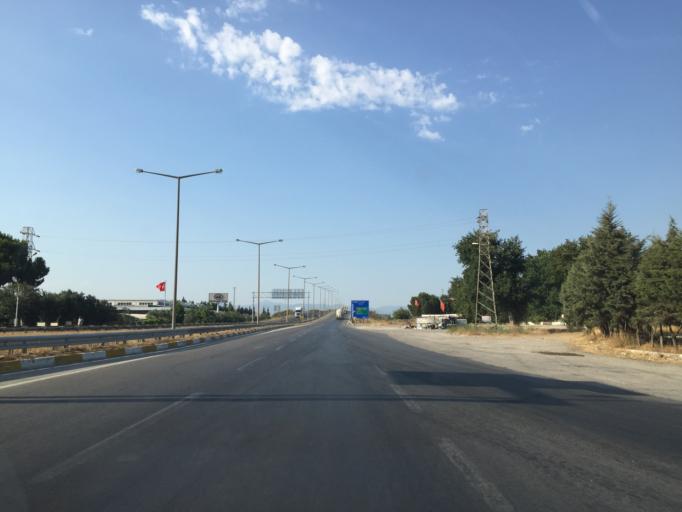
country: TR
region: Izmir
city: Belevi
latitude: 38.0209
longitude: 27.4411
